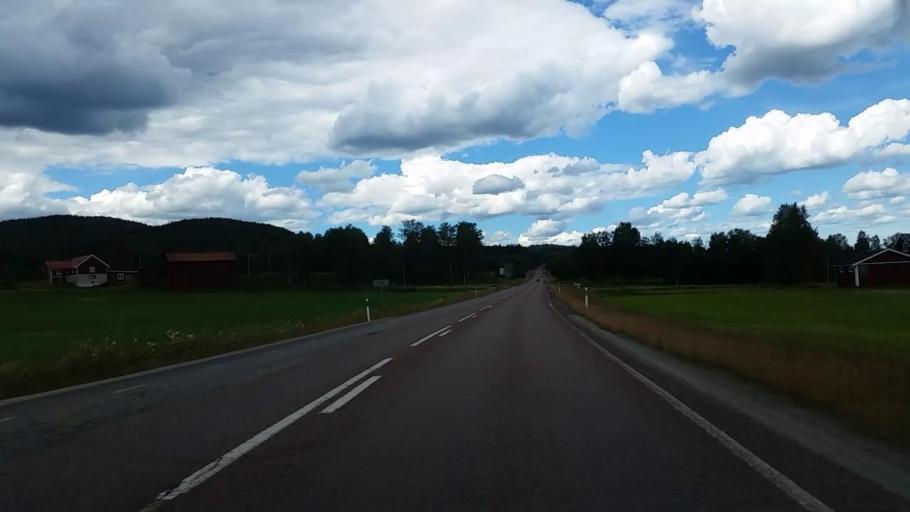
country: SE
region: Gaevleborg
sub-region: Ljusdals Kommun
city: Jaervsoe
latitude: 61.6743
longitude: 16.1449
